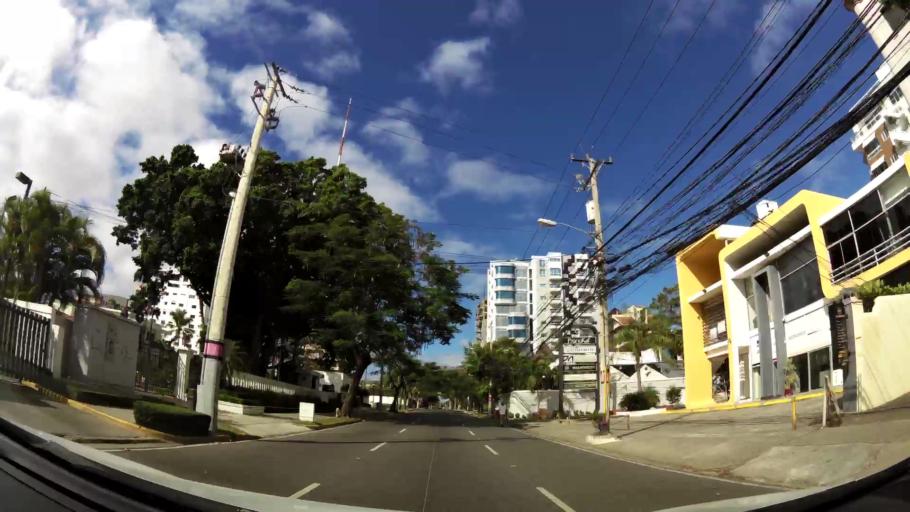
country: DO
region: Nacional
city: La Julia
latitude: 18.4619
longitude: -69.9308
